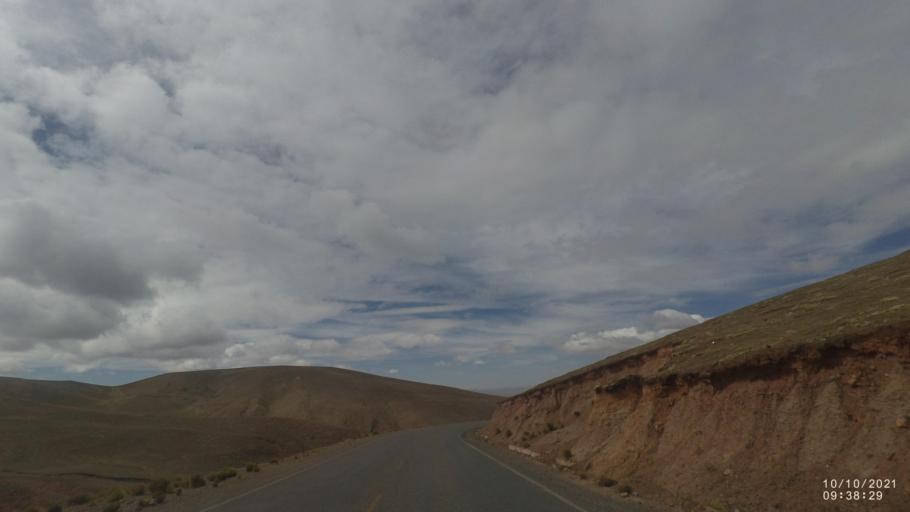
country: BO
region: La Paz
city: Quime
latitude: -17.1334
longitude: -67.3393
